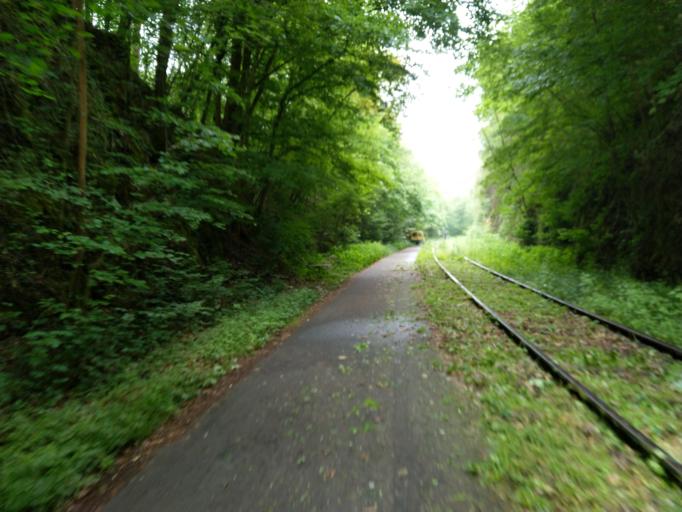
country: BE
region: Wallonia
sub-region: Province de Namur
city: Onhaye
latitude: 50.3022
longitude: 4.7757
